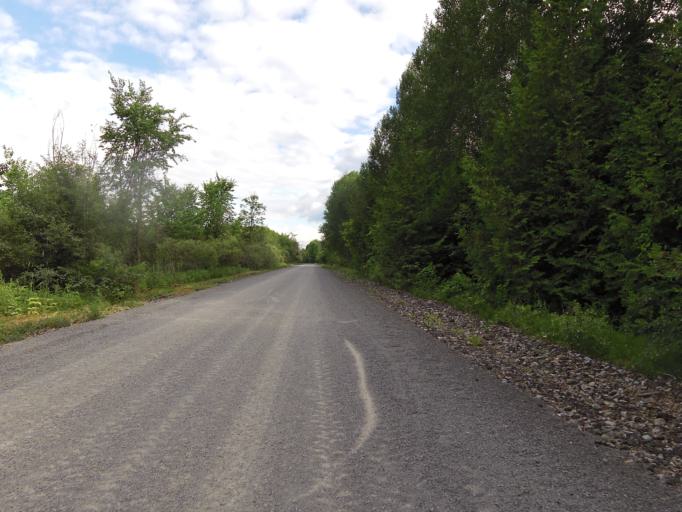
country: CA
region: Ontario
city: Arnprior
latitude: 45.2982
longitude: -76.2632
